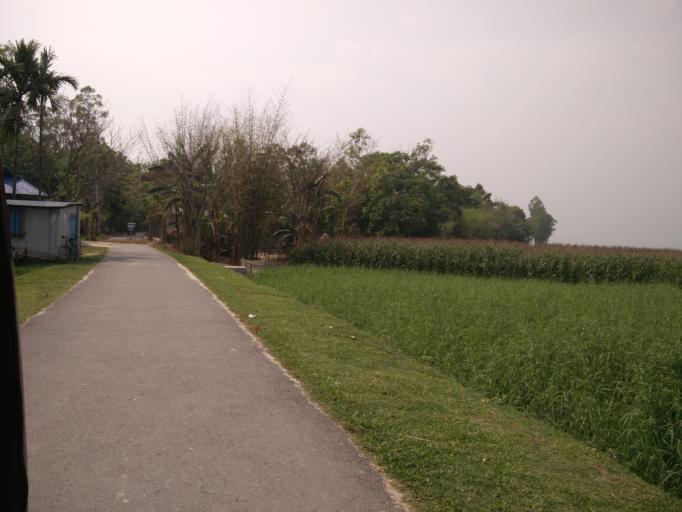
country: BD
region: Dhaka
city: Muktagacha
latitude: 24.9005
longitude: 90.2591
